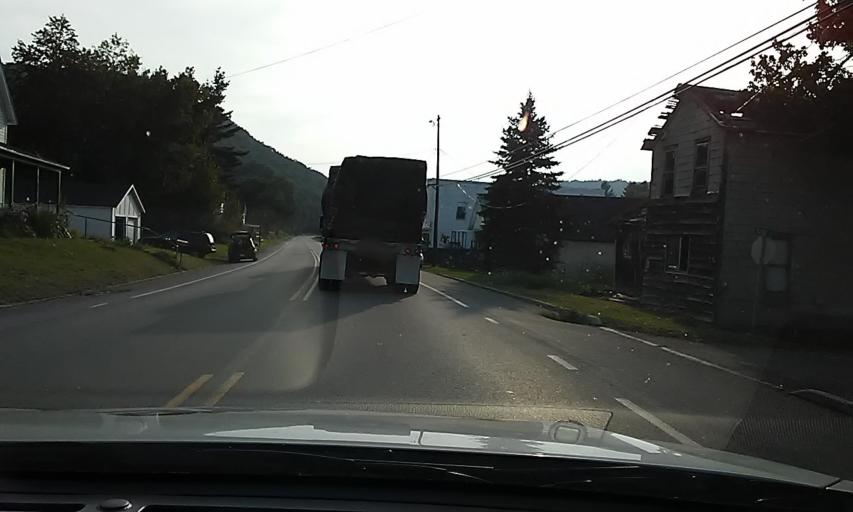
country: US
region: Pennsylvania
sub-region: McKean County
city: Smethport
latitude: 41.7059
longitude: -78.5815
